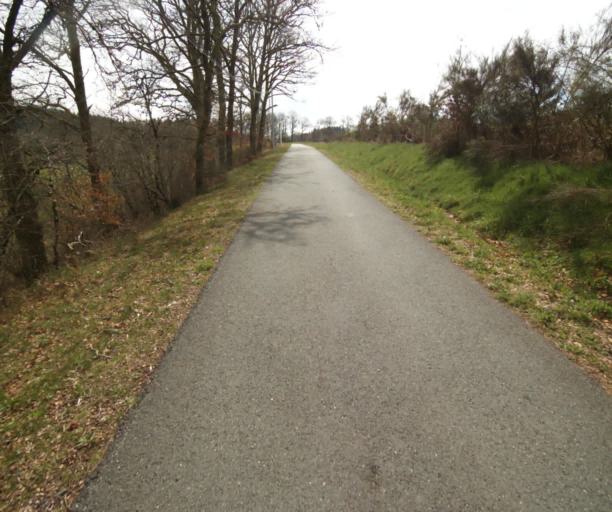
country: FR
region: Limousin
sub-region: Departement de la Correze
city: Egletons
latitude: 45.3681
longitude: 1.9707
